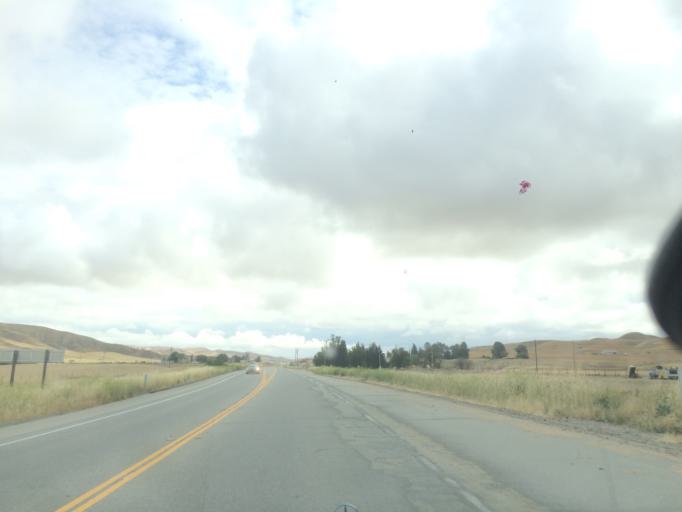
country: US
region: California
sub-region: San Luis Obispo County
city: Shandon
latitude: 35.6642
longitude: -120.3613
